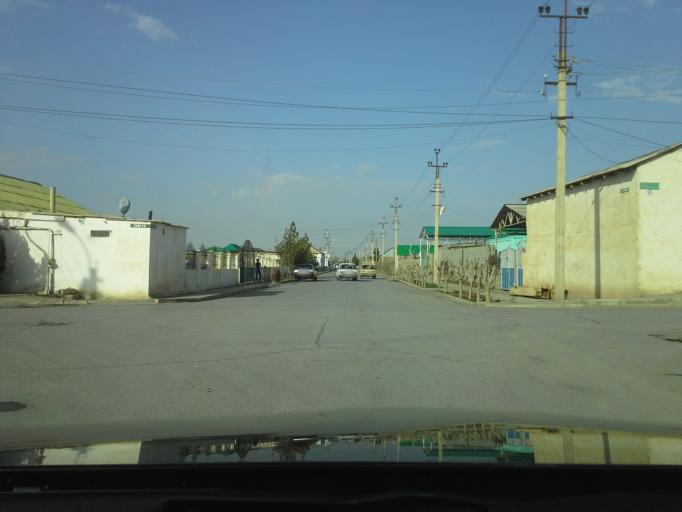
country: TM
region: Ahal
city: Abadan
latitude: 38.0171
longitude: 58.2329
